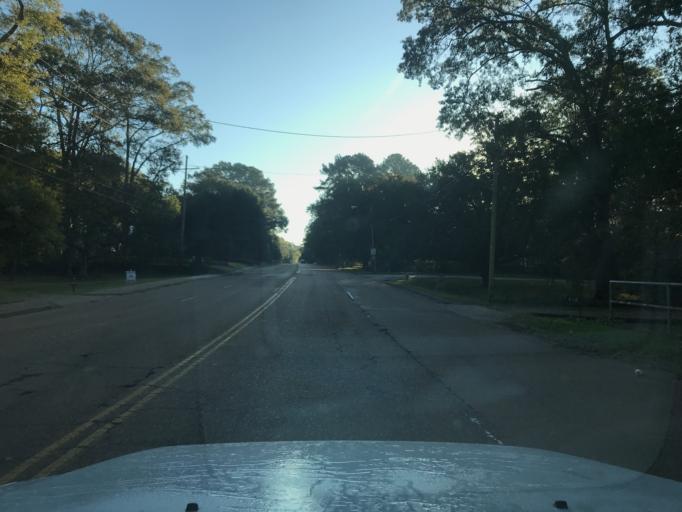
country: US
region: Mississippi
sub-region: Rankin County
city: Flowood
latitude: 32.3503
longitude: -90.1694
